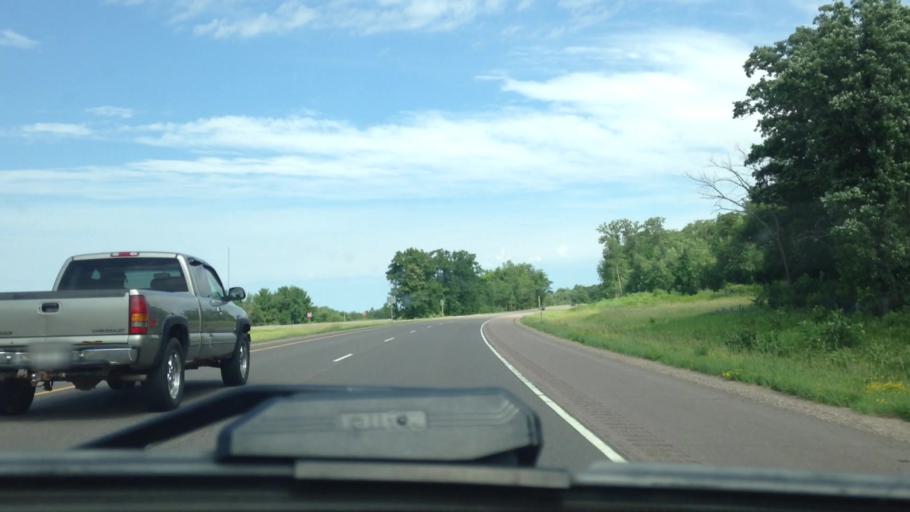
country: US
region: Wisconsin
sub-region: Washburn County
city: Spooner
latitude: 45.8026
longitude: -91.8543
